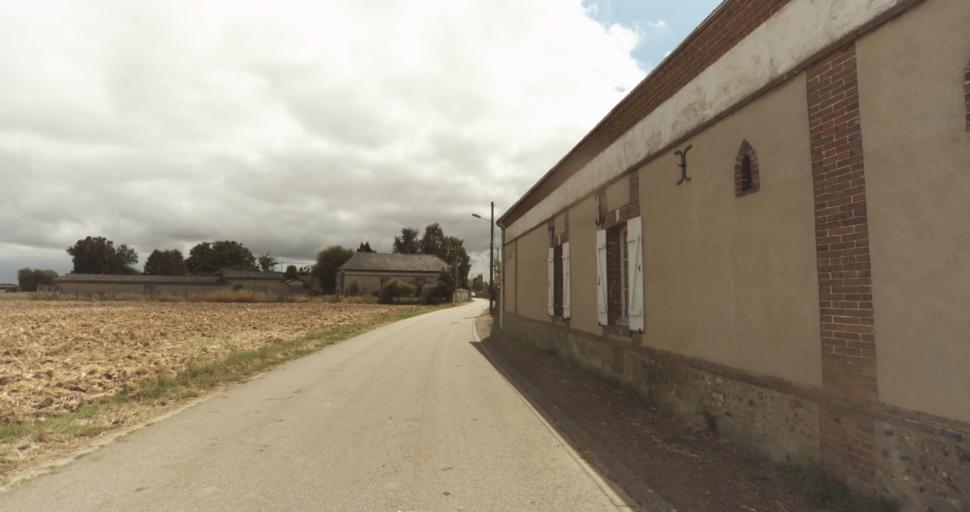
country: FR
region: Haute-Normandie
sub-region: Departement de l'Eure
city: La Madeleine-de-Nonancourt
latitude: 48.9024
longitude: 1.2367
